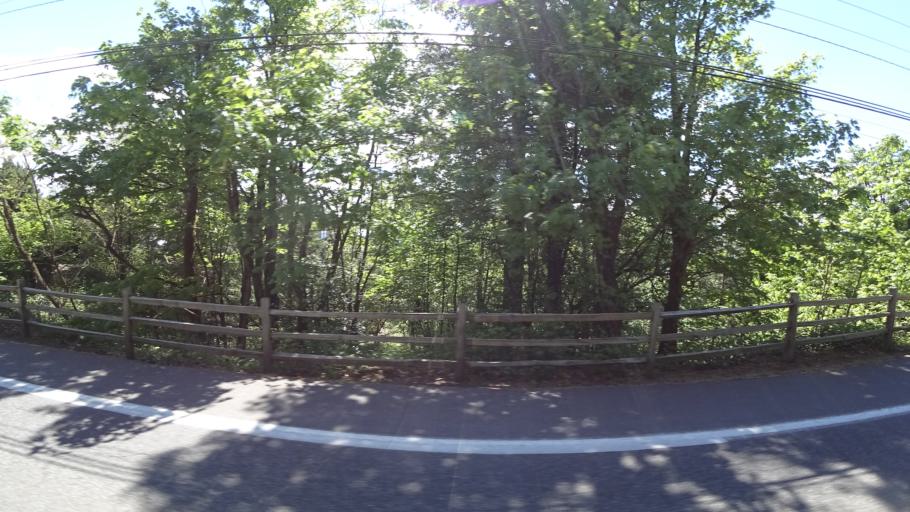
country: US
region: Oregon
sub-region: Washington County
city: West Haven
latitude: 45.5482
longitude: -122.7687
